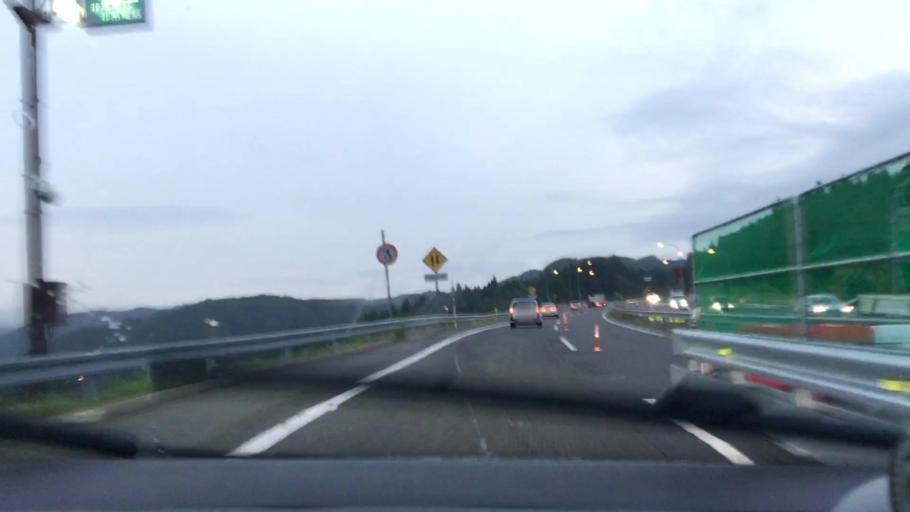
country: JP
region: Gifu
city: Gujo
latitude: 35.9366
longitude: 136.8803
